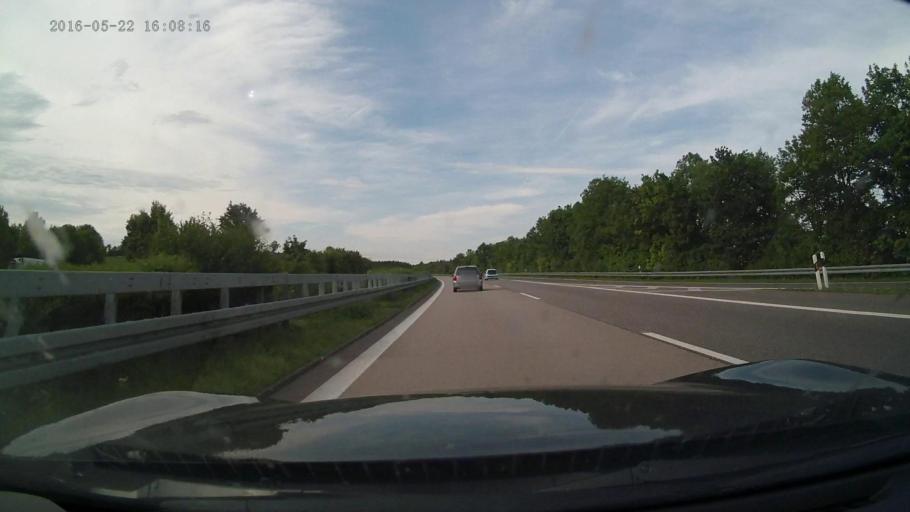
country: DE
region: Baden-Wuerttemberg
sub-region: Regierungsbezirk Stuttgart
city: Widdern
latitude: 49.3249
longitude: 9.4141
